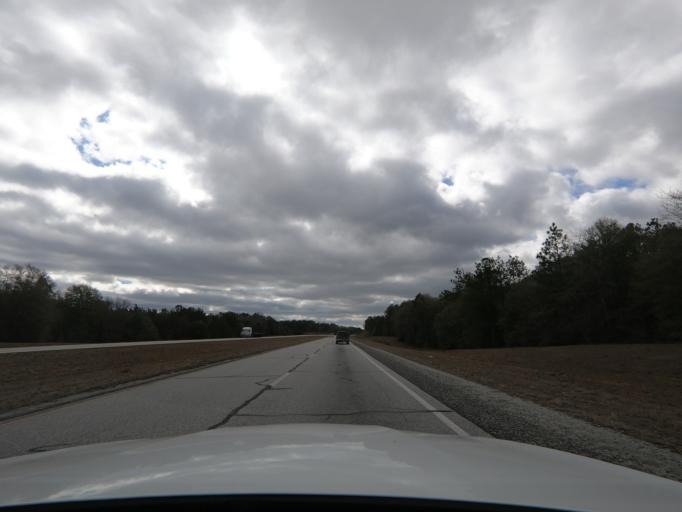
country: US
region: Alabama
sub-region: Russell County
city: Ladonia
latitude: 32.3154
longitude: -85.1771
